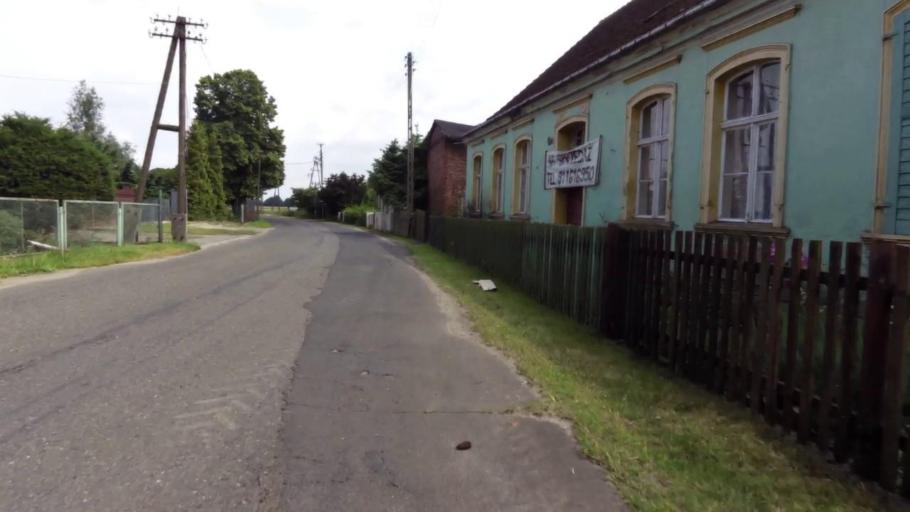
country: PL
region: West Pomeranian Voivodeship
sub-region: Powiat goleniowski
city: Stepnica
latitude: 53.6689
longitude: 14.5783
